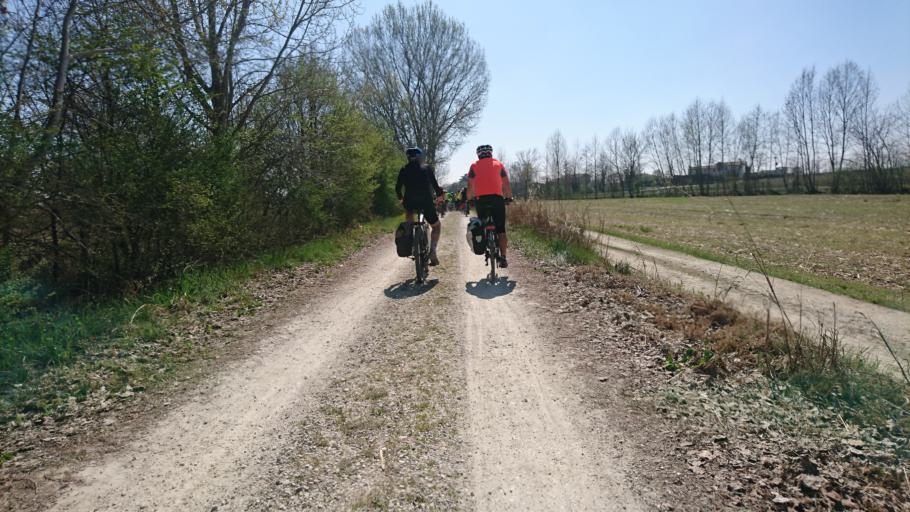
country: IT
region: Veneto
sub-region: Provincia di Padova
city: Piazzola sul Brenta
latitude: 45.5677
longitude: 11.7607
